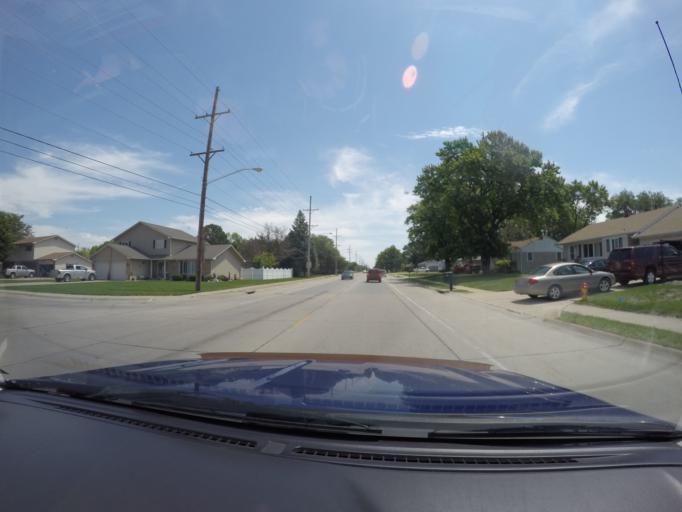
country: US
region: Nebraska
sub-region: Hall County
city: Grand Island
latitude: 40.9015
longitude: -98.3519
